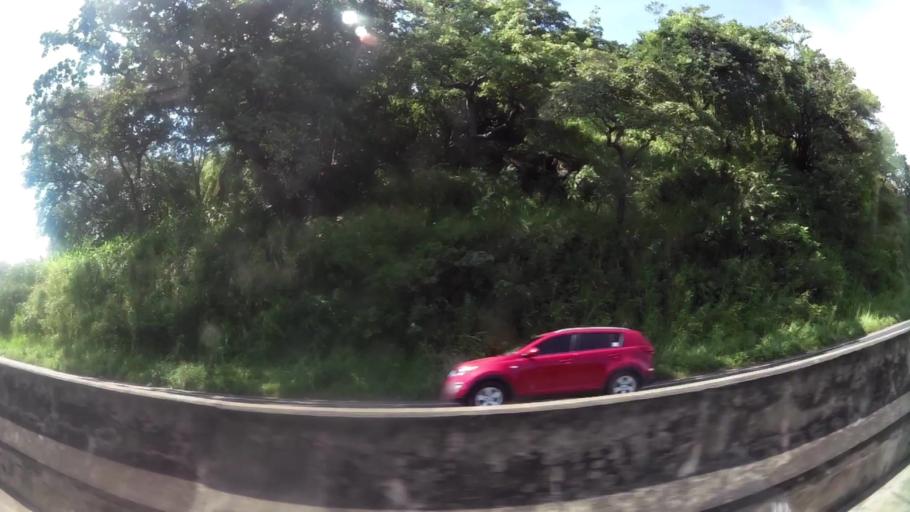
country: PA
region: Panama
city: Bejuco
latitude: 8.6429
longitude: -79.8749
